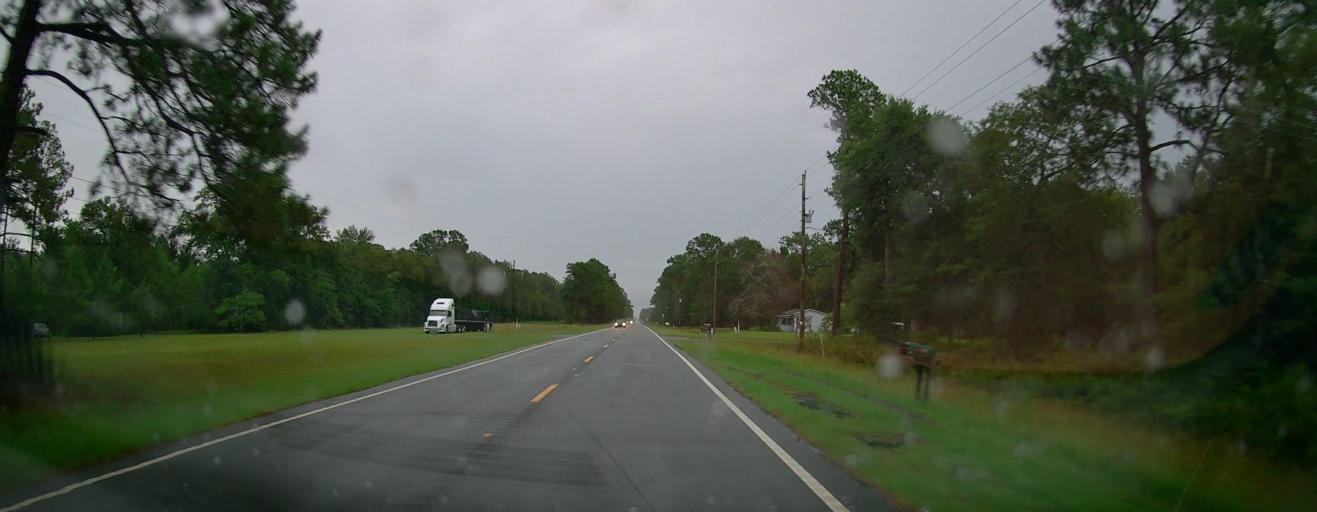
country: US
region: Georgia
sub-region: Brantley County
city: Nahunta
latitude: 31.3313
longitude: -81.9195
